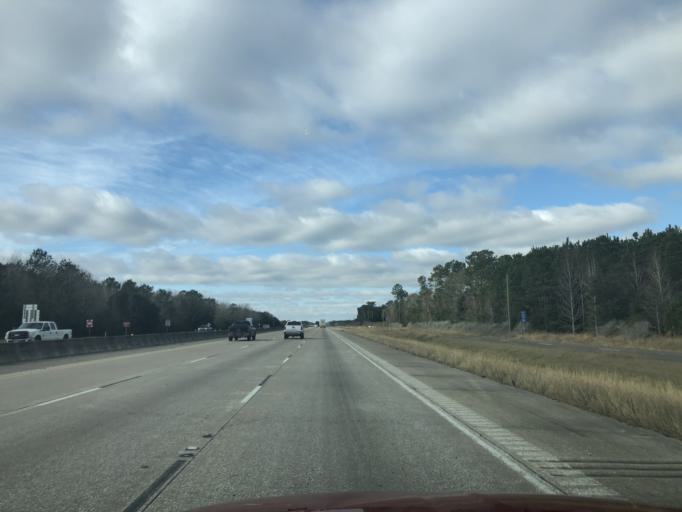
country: US
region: Texas
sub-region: Chambers County
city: Anahuac
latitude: 29.8377
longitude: -94.5816
